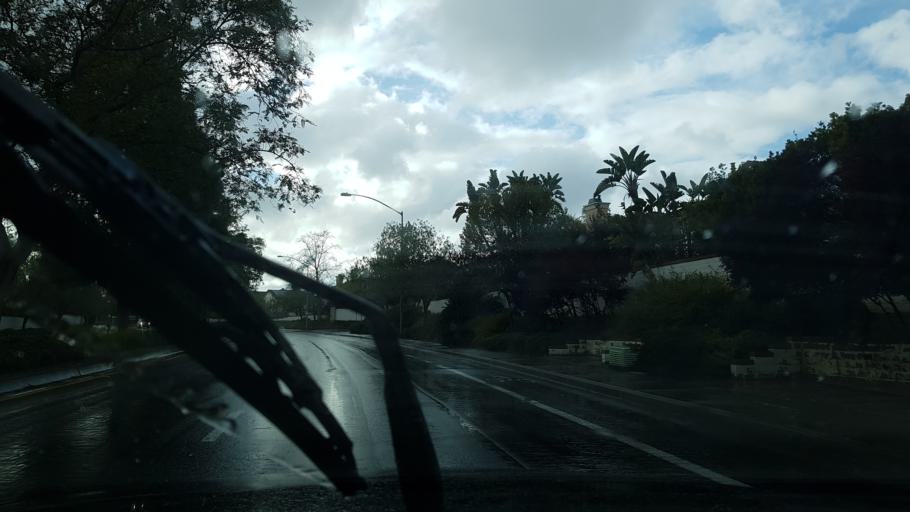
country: US
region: California
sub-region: San Diego County
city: Fairbanks Ranch
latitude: 32.9293
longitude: -117.1942
